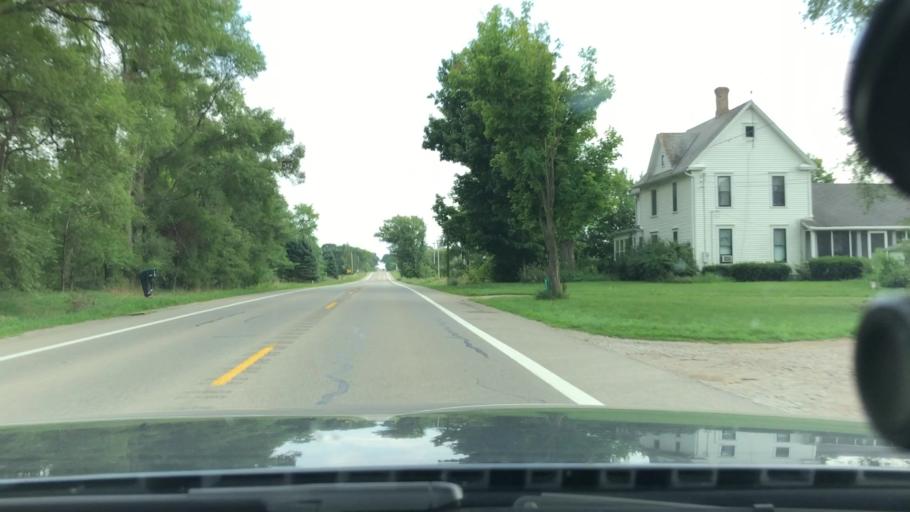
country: US
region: Michigan
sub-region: Washtenaw County
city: Manchester
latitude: 42.2046
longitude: -84.0328
